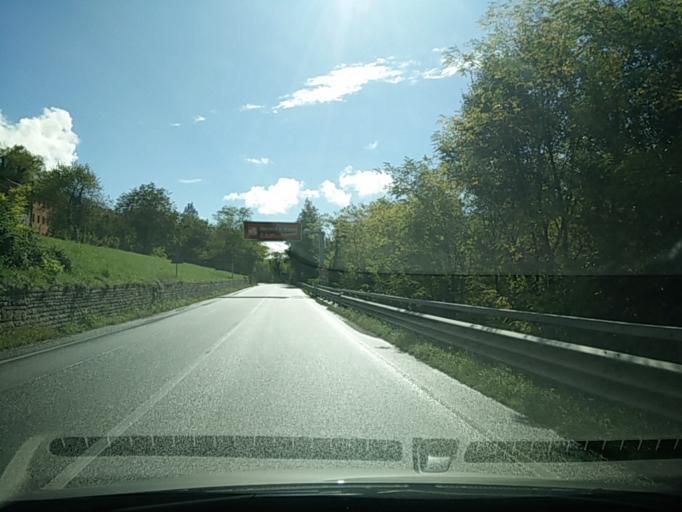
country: IT
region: Veneto
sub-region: Provincia di Treviso
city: Segusino
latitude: 45.8994
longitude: 11.9519
